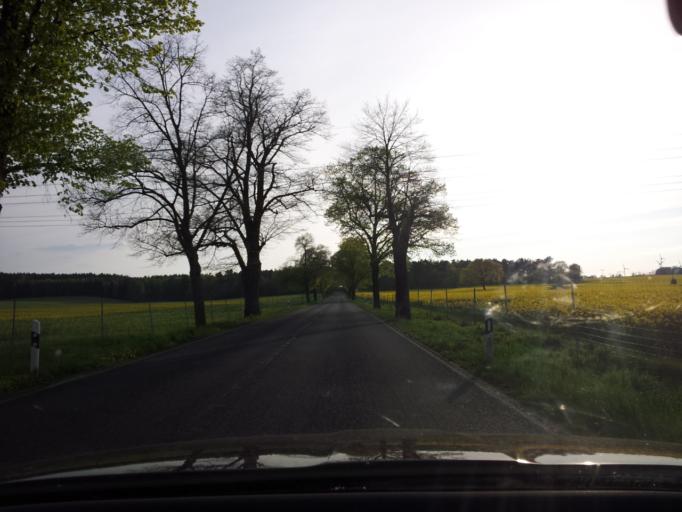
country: DE
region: Brandenburg
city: Drahnsdorf
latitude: 51.8530
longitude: 13.5984
